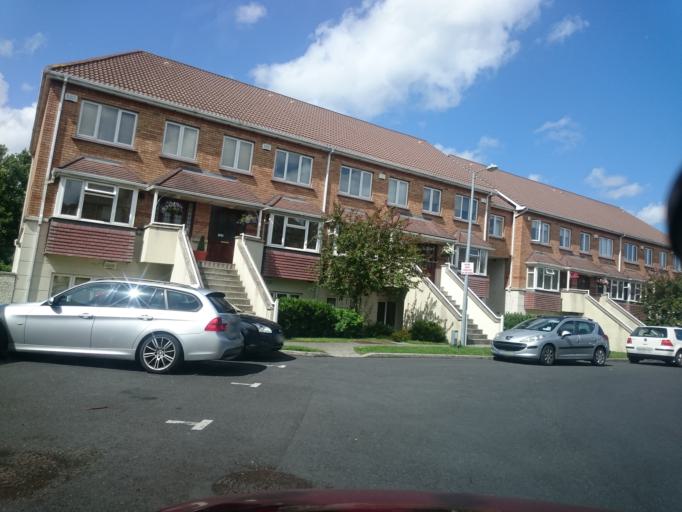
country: IE
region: Leinster
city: Clondalkin
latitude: 53.3093
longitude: -6.4079
